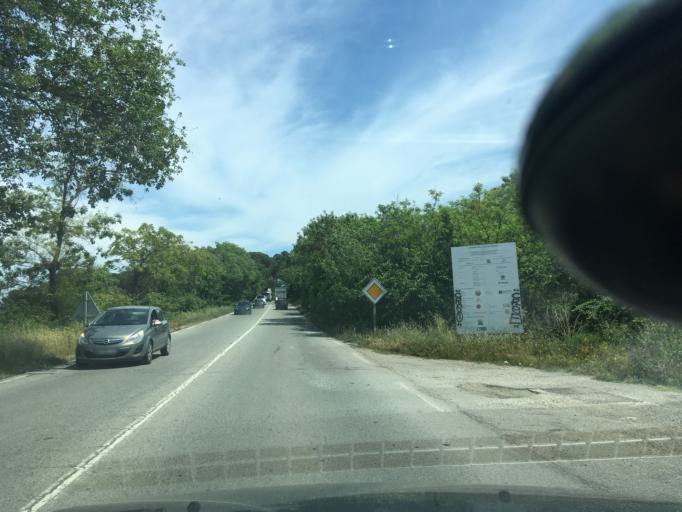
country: FR
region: Provence-Alpes-Cote d'Azur
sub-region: Departement du Var
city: Puget-sur-Argens
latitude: 43.4613
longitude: 6.6589
